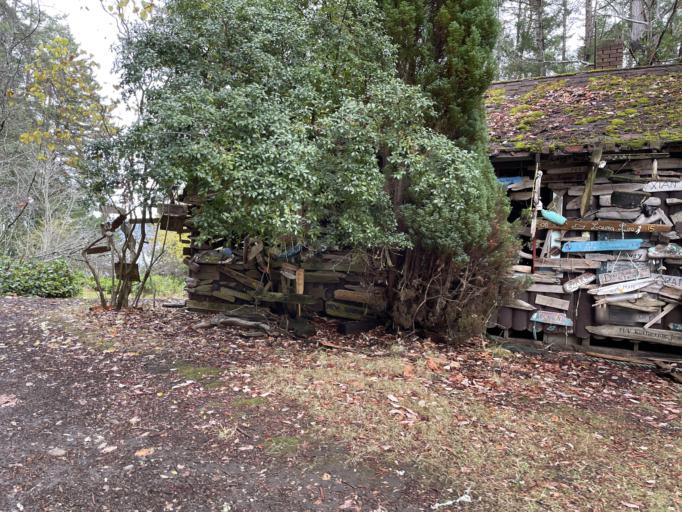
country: CA
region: British Columbia
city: North Cowichan
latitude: 48.9380
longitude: -123.5443
